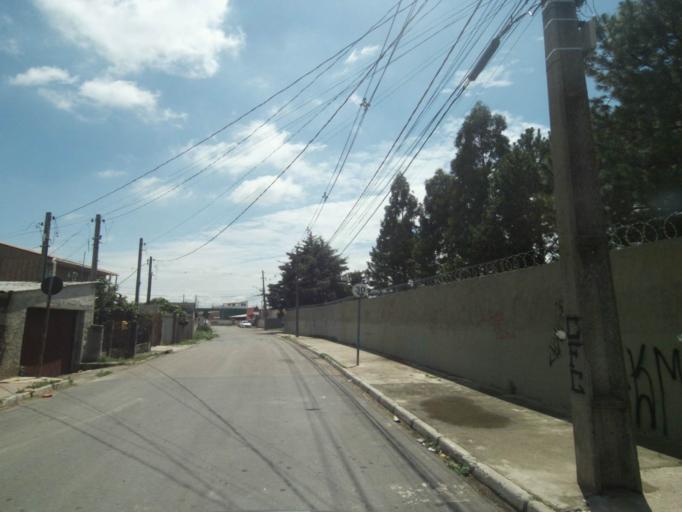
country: BR
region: Parana
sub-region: Pinhais
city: Pinhais
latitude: -25.4727
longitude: -49.1885
